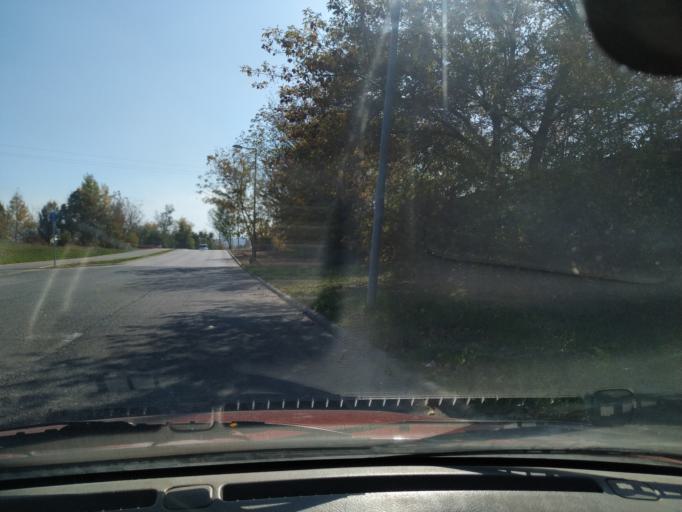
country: HU
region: Komarom-Esztergom
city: Esztergom
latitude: 47.7780
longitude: 18.7485
